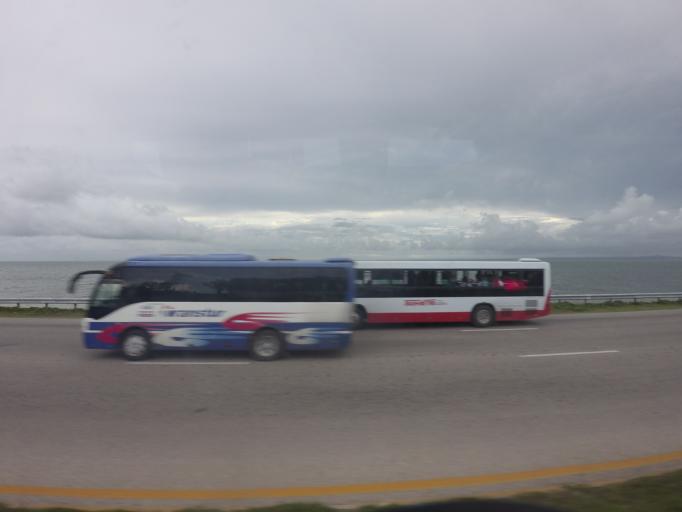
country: CU
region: Matanzas
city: Varadero
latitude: 23.1714
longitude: -81.2101
